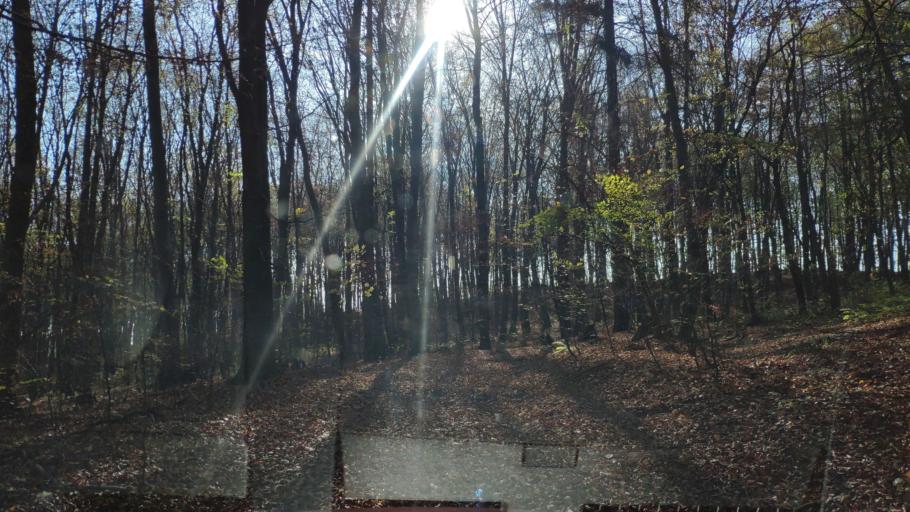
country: SK
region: Presovsky
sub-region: Okres Presov
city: Presov
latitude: 48.8979
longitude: 21.2251
